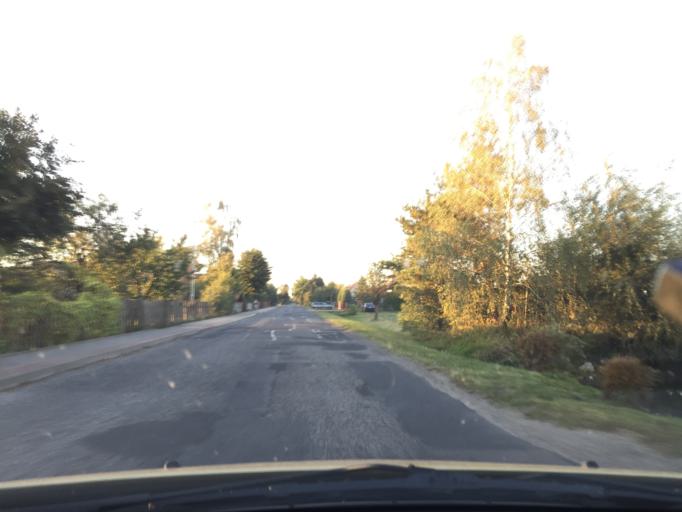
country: PL
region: Greater Poland Voivodeship
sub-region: Powiat pleszewski
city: Dobrzyca
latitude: 51.8123
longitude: 17.6225
